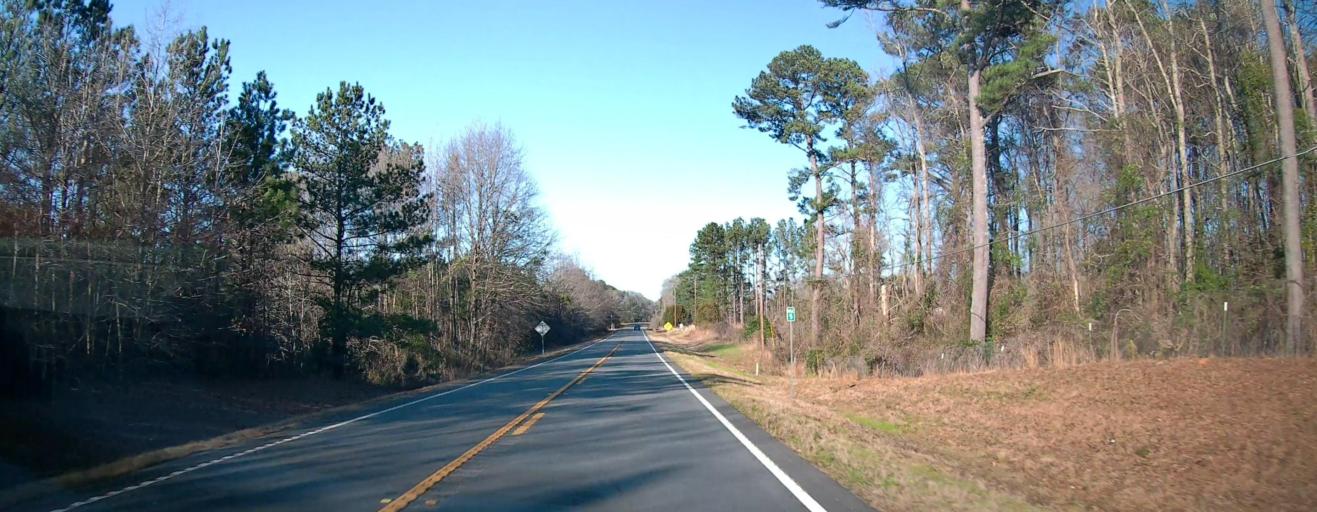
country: US
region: Georgia
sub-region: Meriwether County
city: Manchester
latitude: 32.9052
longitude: -84.6791
